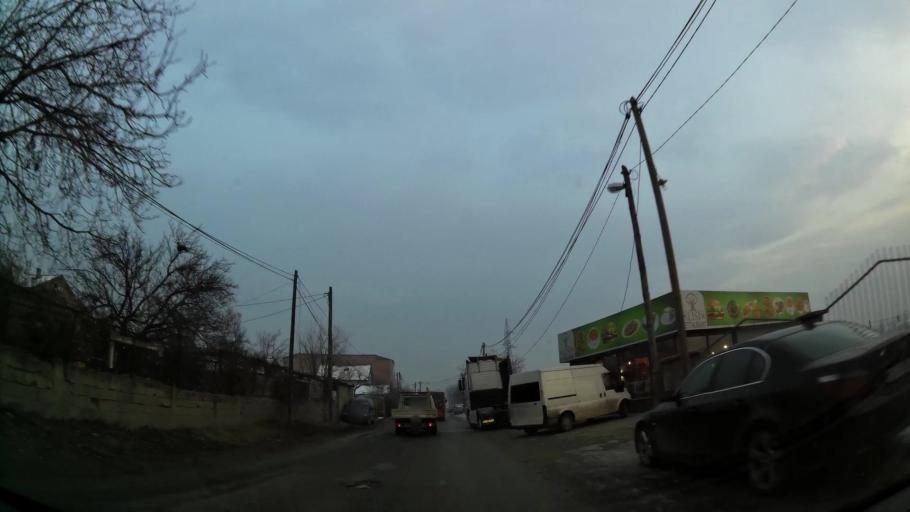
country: MK
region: Suto Orizari
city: Suto Orizare
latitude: 42.0265
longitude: 21.4107
